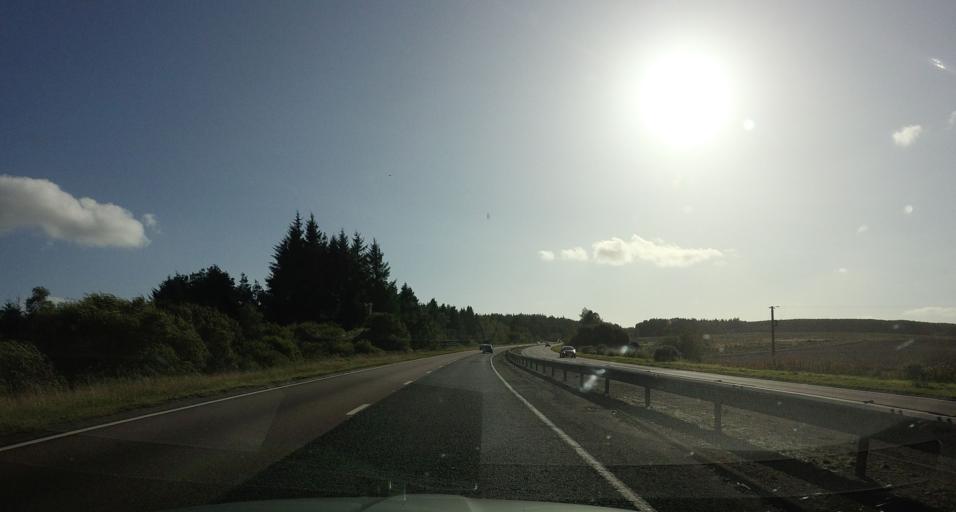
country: GB
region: Scotland
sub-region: Angus
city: Forfar
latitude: 56.5587
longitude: -2.9238
